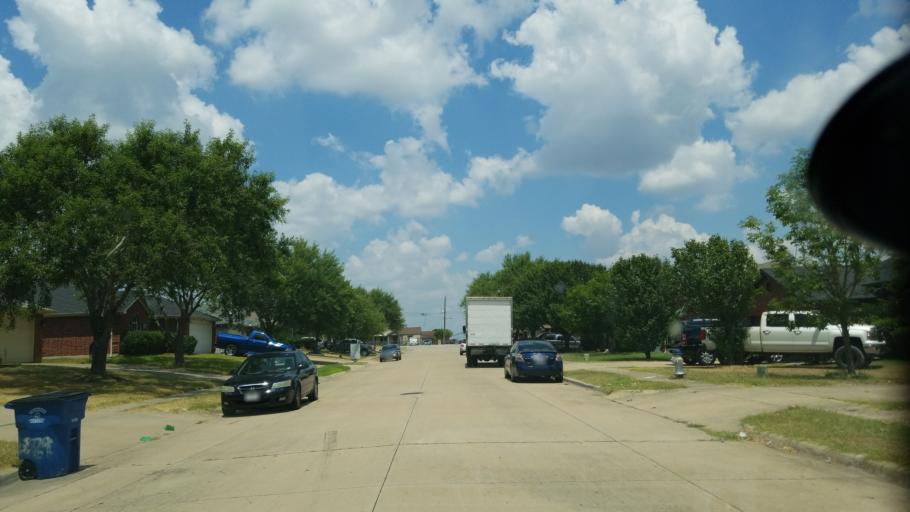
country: US
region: Texas
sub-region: Dallas County
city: Duncanville
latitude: 32.6801
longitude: -96.8993
